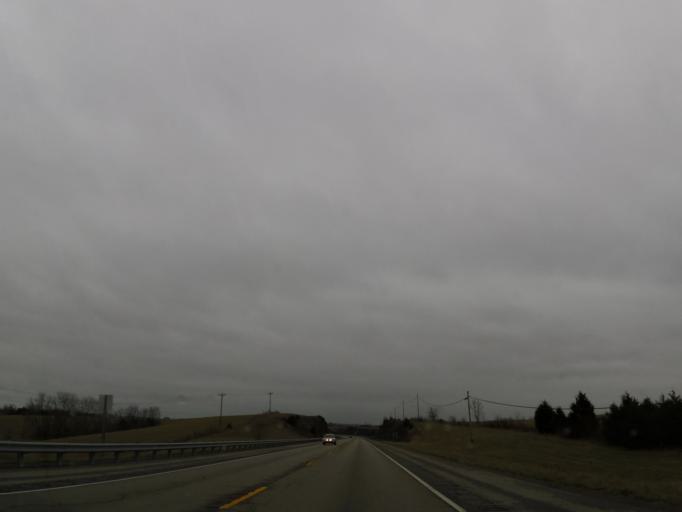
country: US
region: Kentucky
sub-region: Lincoln County
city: Stanford
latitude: 37.4969
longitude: -84.5577
